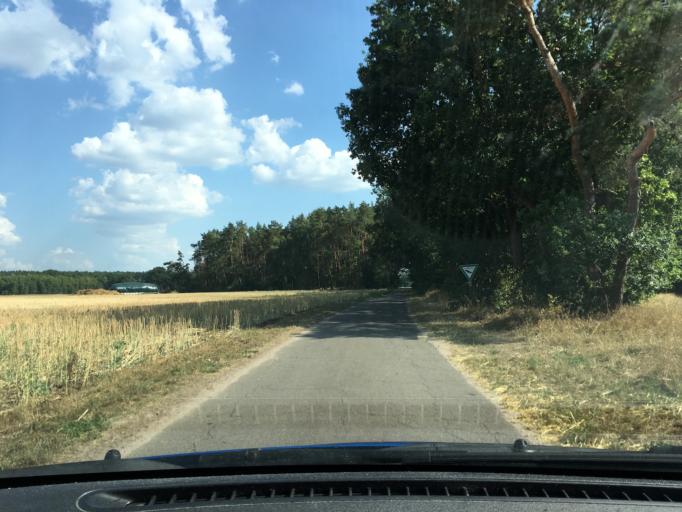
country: DE
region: Lower Saxony
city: Salzhausen
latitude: 53.2167
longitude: 10.2042
